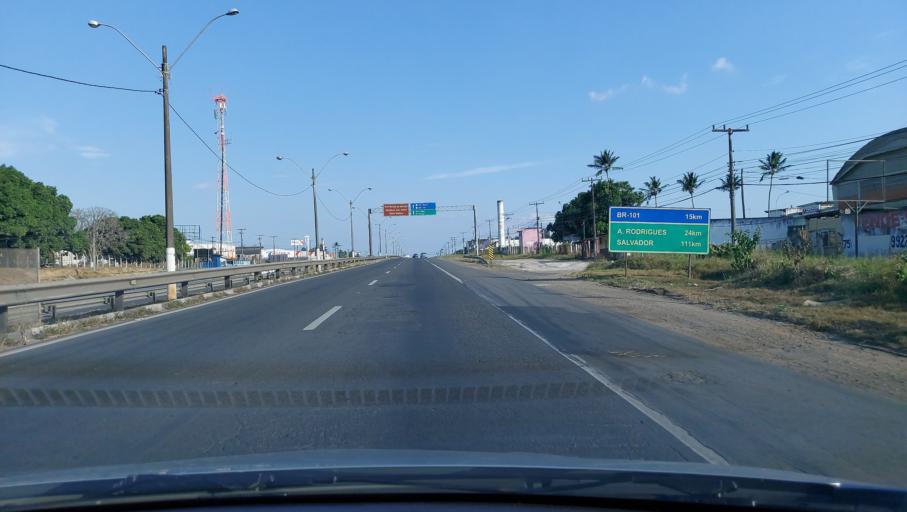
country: BR
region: Bahia
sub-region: Feira De Santana
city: Feira de Santana
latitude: -12.2794
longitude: -38.9262
